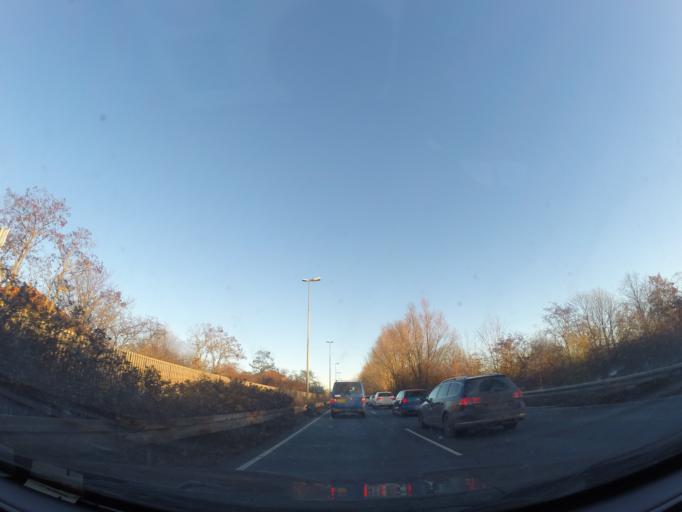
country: DK
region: Capital Region
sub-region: Ballerup Kommune
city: Ballerup
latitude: 55.7237
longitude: 12.3678
